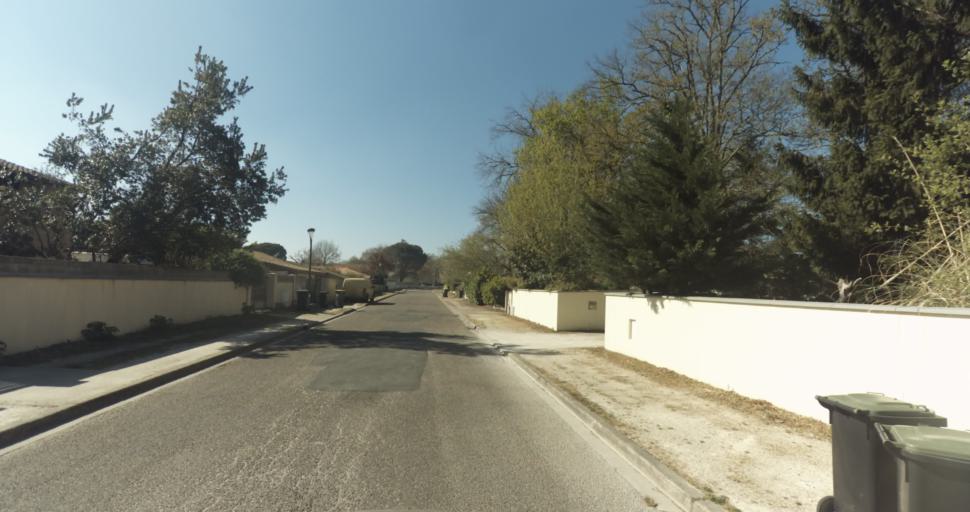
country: FR
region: Aquitaine
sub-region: Departement de la Gironde
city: Martignas-sur-Jalle
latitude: 44.8068
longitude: -0.7913
